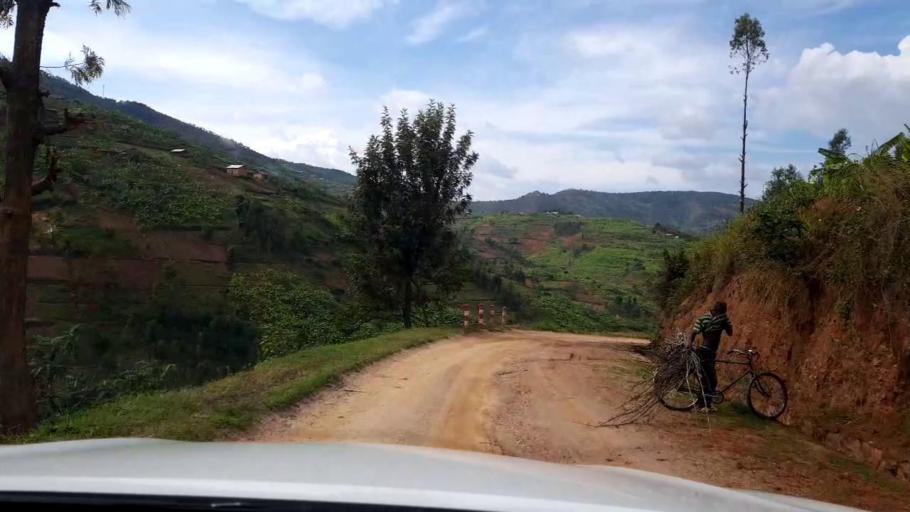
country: RW
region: Southern Province
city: Gitarama
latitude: -1.9781
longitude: 29.7083
